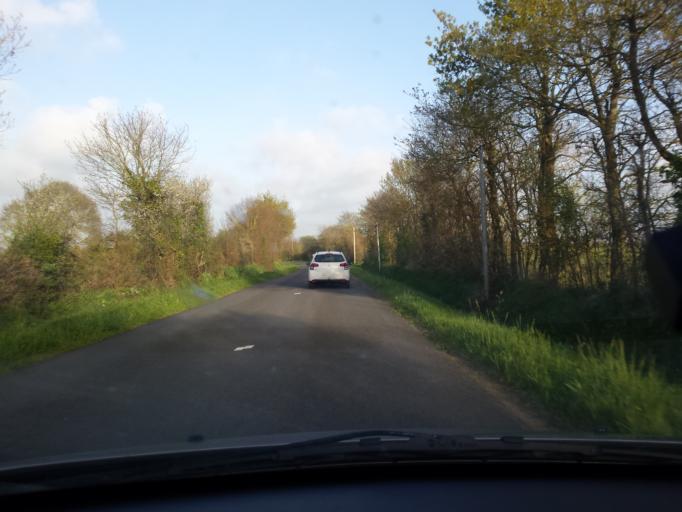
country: FR
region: Pays de la Loire
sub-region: Departement de la Vendee
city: Saint-Mathurin
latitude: 46.5652
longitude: -1.7269
